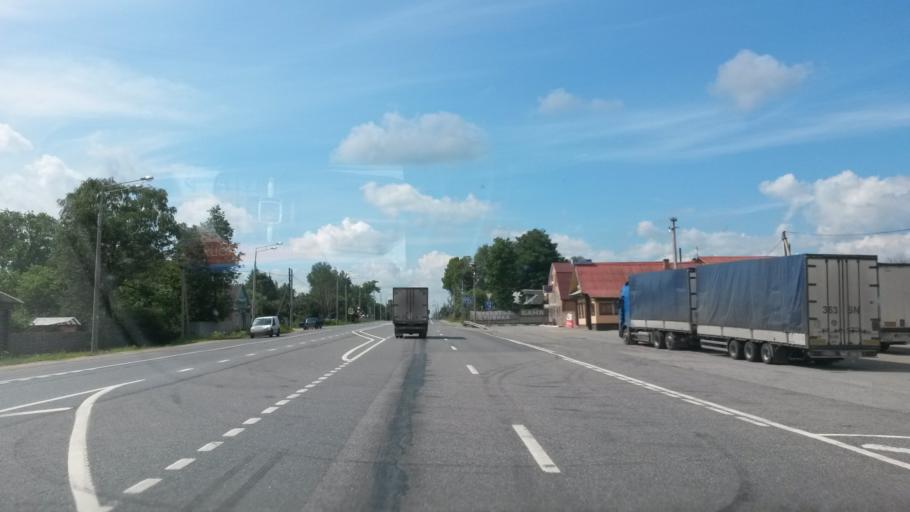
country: RU
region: Jaroslavl
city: Petrovsk
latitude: 56.9384
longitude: 39.1614
